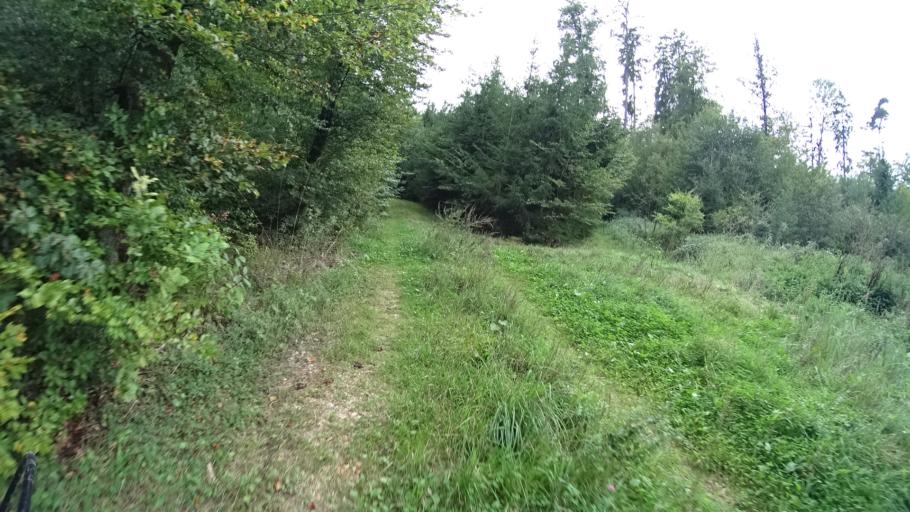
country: DE
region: Bavaria
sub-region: Upper Bavaria
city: Hitzhofen
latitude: 48.8871
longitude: 11.3278
